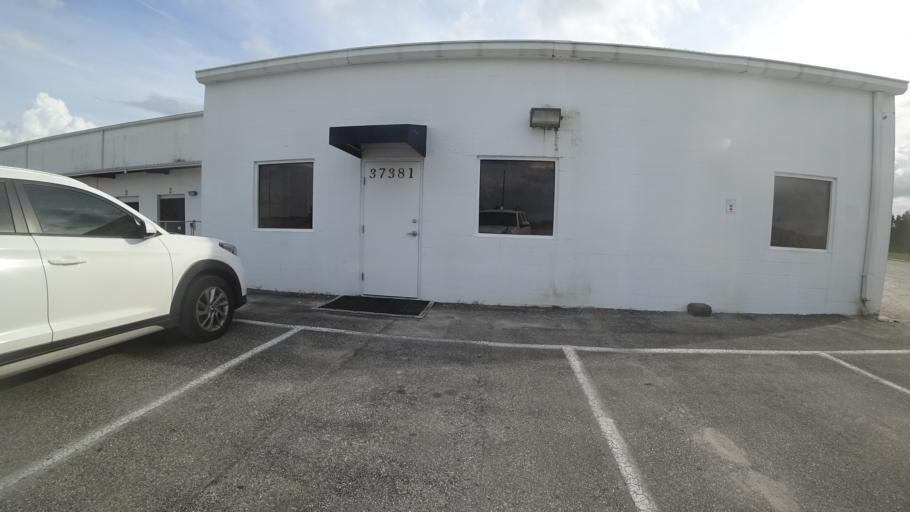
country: US
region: Florida
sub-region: Hillsborough County
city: Wimauma
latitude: 27.5862
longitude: -82.1587
